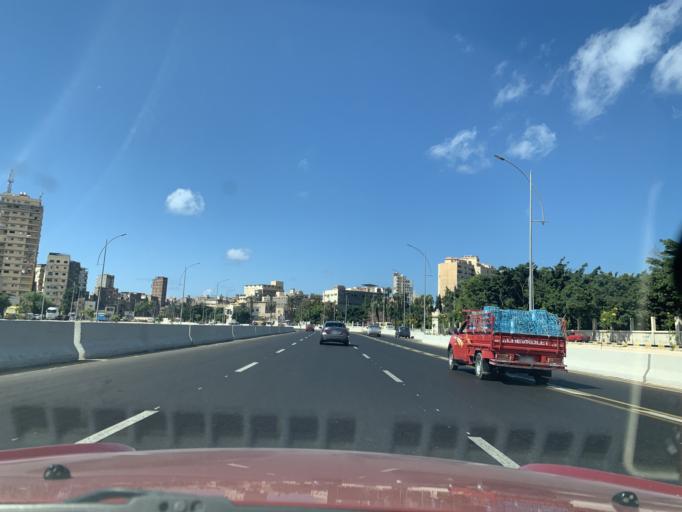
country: EG
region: Alexandria
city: Alexandria
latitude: 31.2018
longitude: 29.9445
